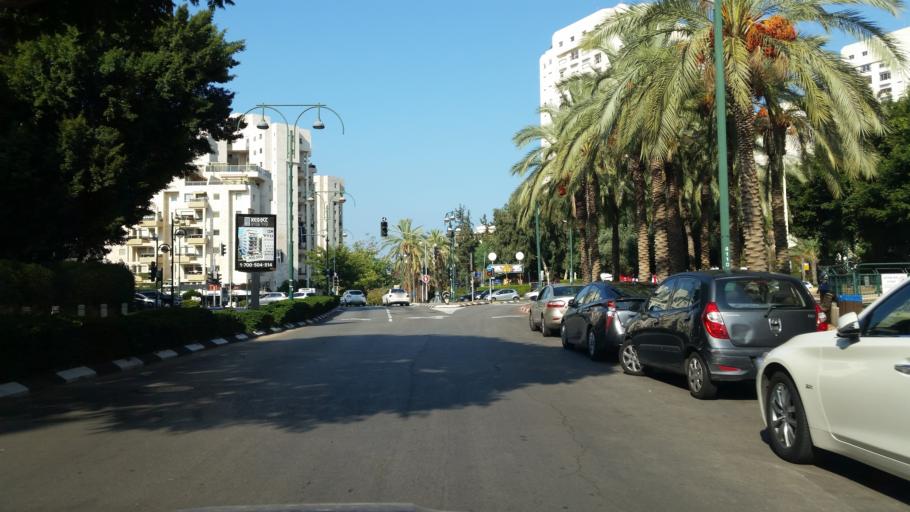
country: IL
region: Tel Aviv
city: Ramat HaSharon
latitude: 32.1514
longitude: 34.8427
